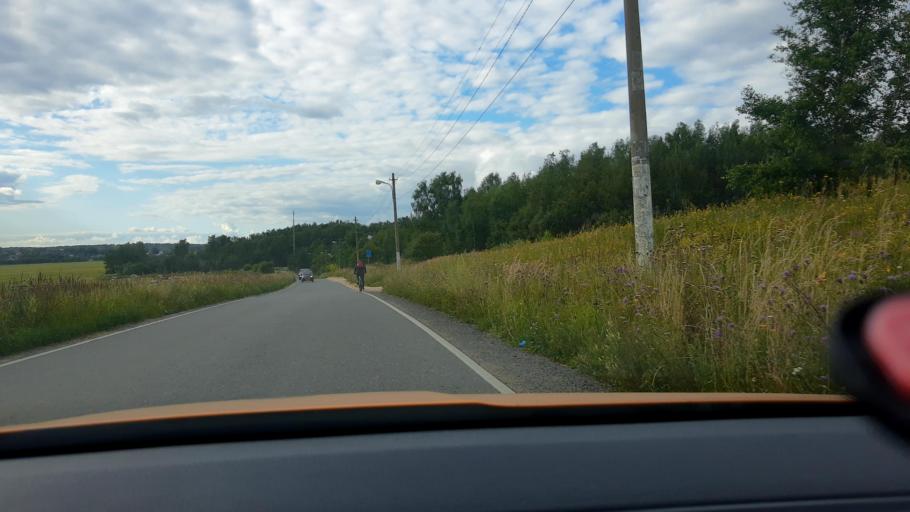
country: RU
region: Moskovskaya
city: Nikolina Gora
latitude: 55.7427
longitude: 36.9875
